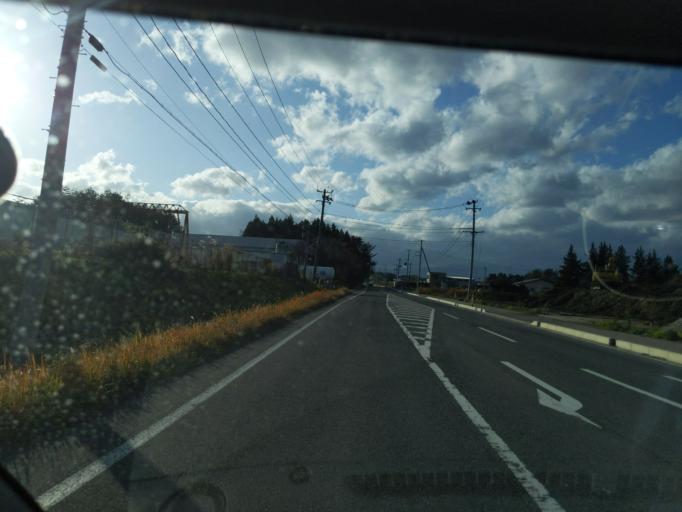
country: JP
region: Iwate
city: Mizusawa
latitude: 39.1130
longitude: 141.0758
